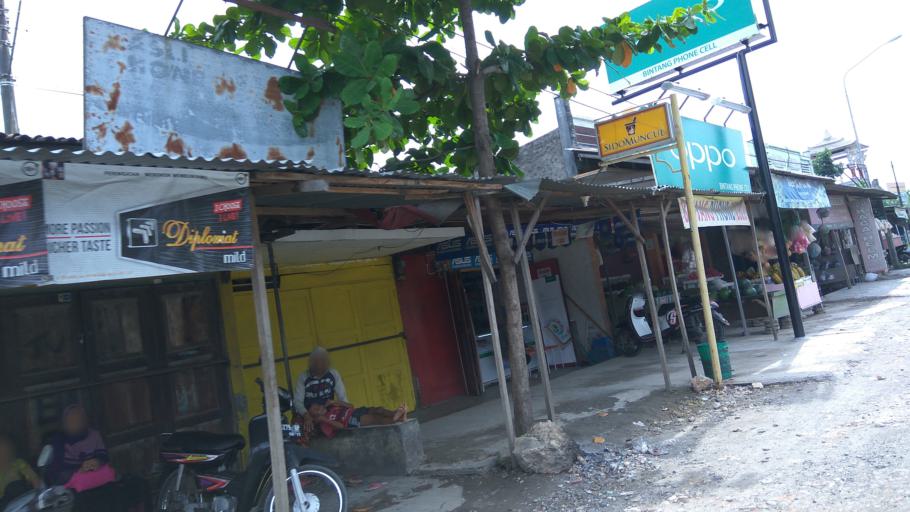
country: ID
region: Central Java
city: Mranggen
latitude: -7.0497
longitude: 110.5995
